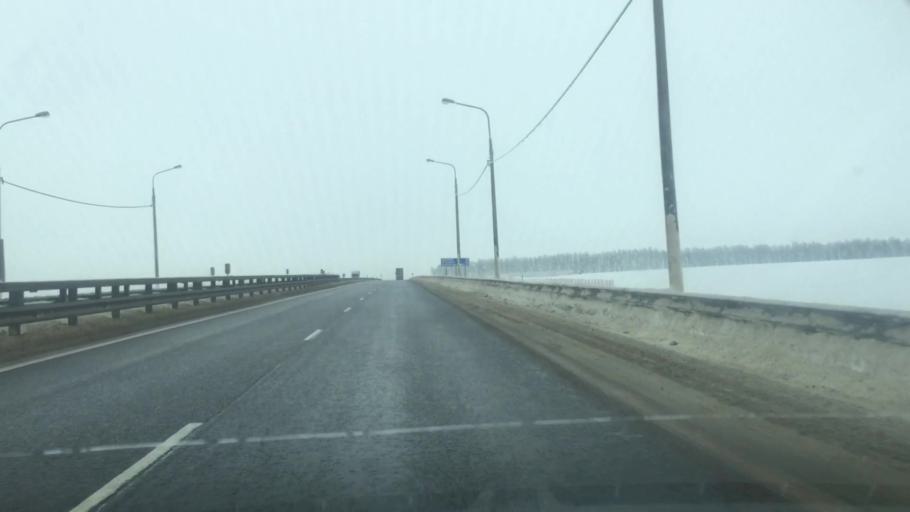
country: RU
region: Lipetsk
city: Stanovoye
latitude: 52.7950
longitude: 38.3314
